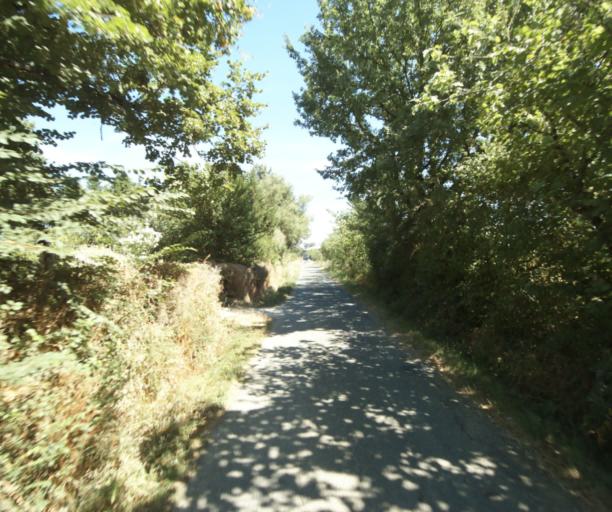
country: FR
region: Midi-Pyrenees
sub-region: Departement de la Haute-Garonne
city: Saint-Felix-Lauragais
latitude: 43.5130
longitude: 1.9071
